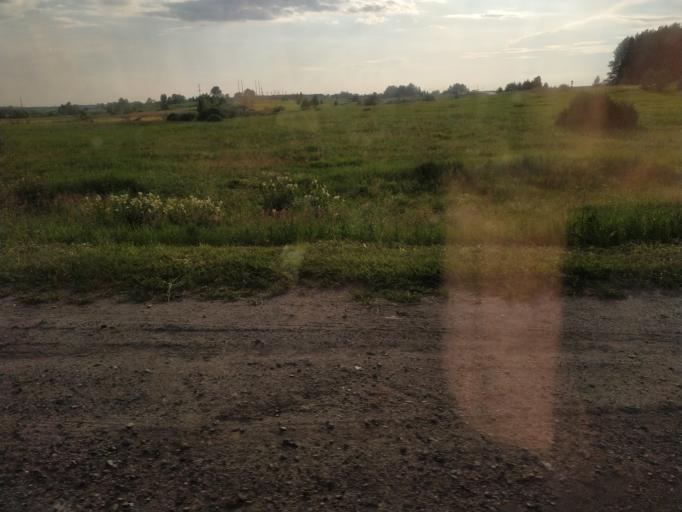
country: RU
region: Sverdlovsk
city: Kamyshlov
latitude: 57.0130
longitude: 62.7231
